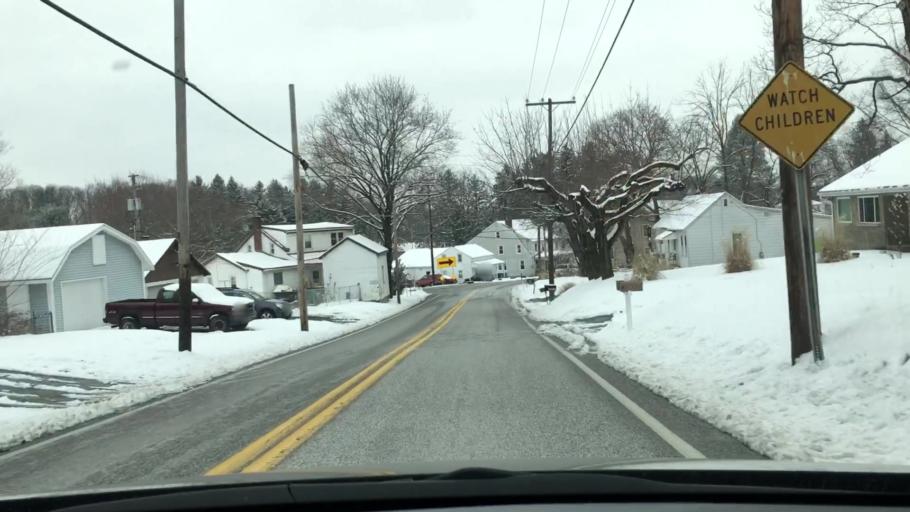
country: US
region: Pennsylvania
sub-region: York County
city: Emigsville
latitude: 40.0006
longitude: -76.7059
